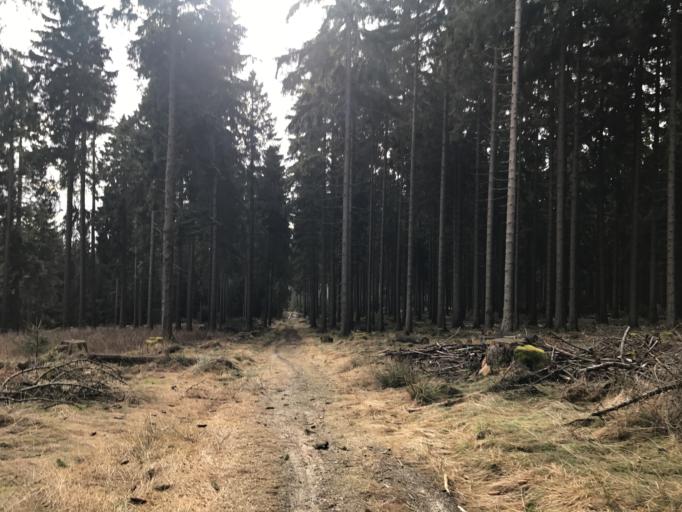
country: DE
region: Hesse
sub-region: Regierungsbezirk Darmstadt
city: Glashutten
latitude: 50.2159
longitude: 8.4436
